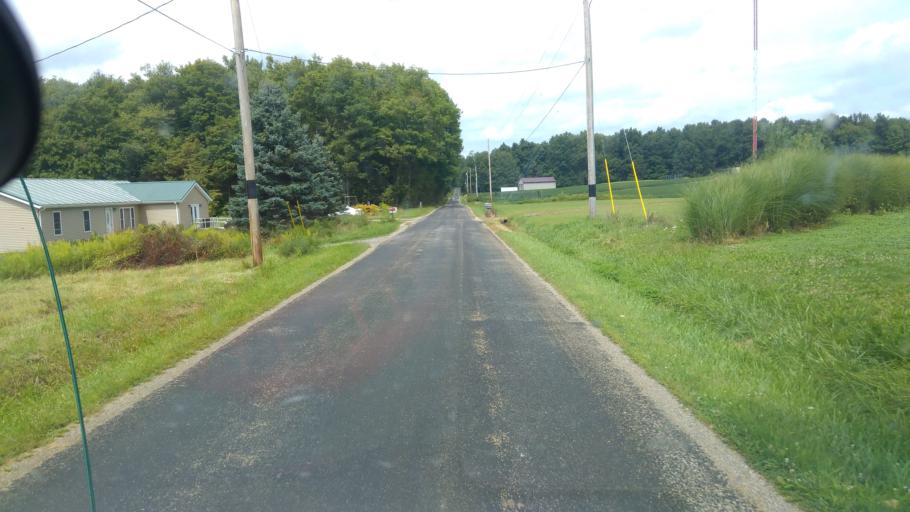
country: US
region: Ohio
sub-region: Ashland County
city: Ashland
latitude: 40.7958
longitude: -82.3690
